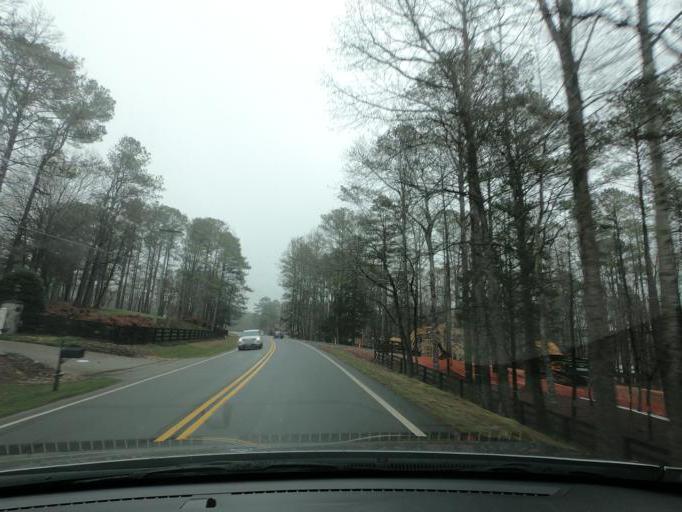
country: US
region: Georgia
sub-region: Fulton County
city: Milton
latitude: 34.1162
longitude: -84.3092
